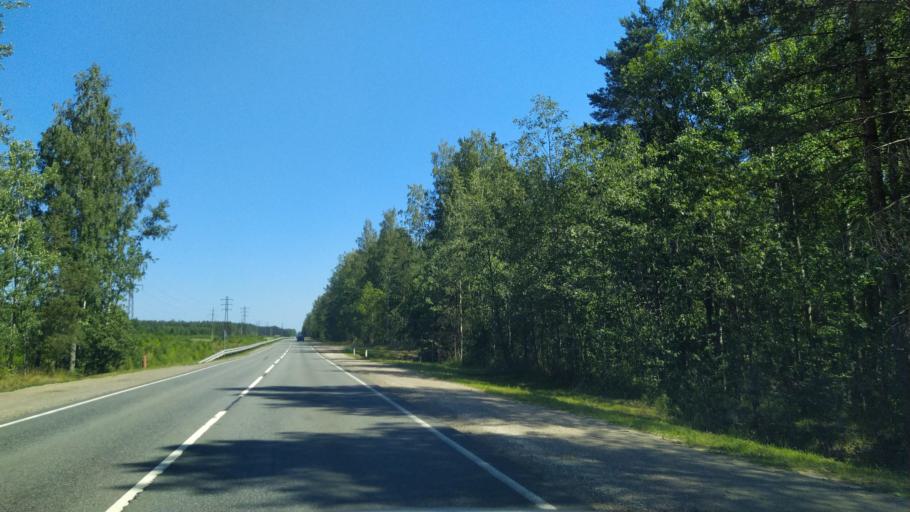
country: RU
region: Leningrad
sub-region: Volosovskiy Rayon
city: Shlissel'burg
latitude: 59.9511
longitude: 30.9904
